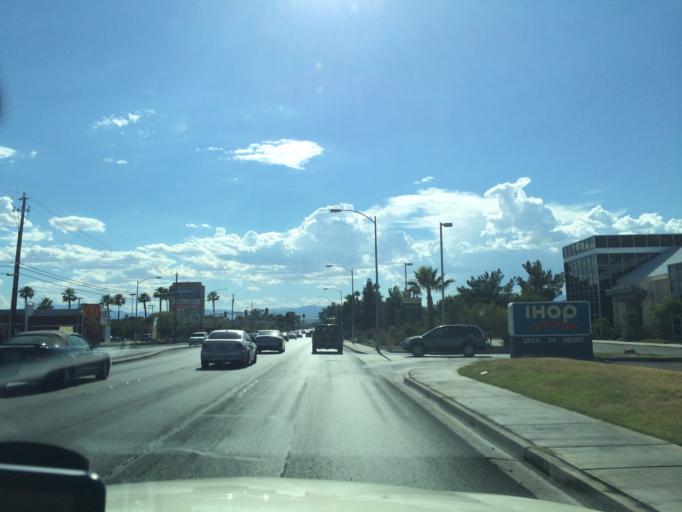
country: US
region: Nevada
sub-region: Clark County
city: Winchester
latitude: 36.1001
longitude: -115.1039
